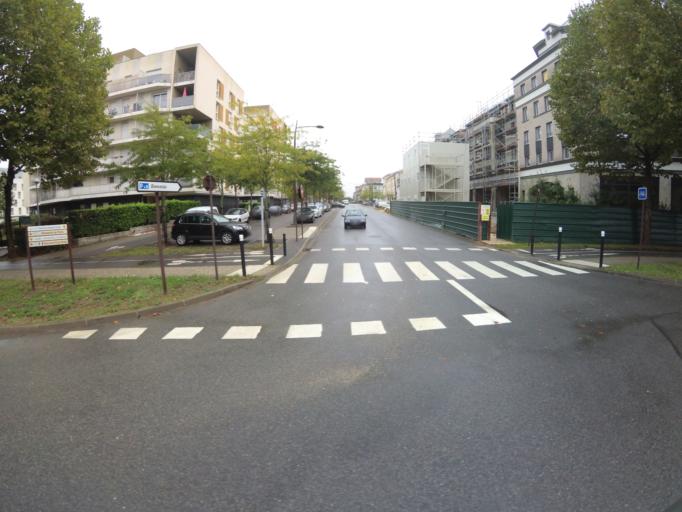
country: FR
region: Ile-de-France
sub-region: Departement de Seine-et-Marne
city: Bussy-Saint-Georges
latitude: 48.8347
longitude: 2.7064
